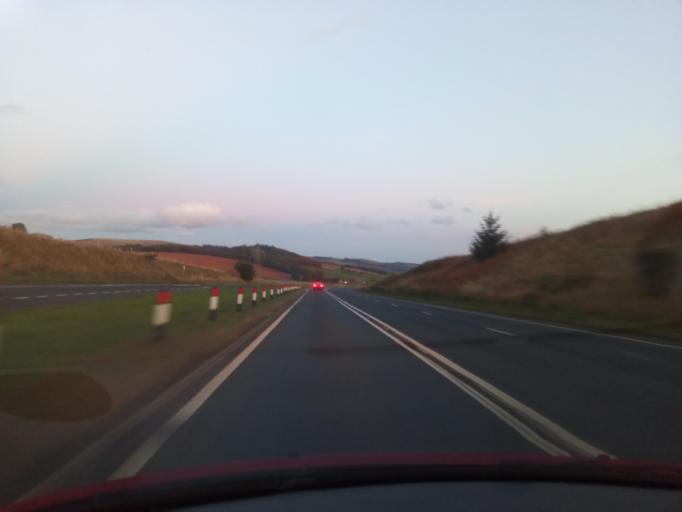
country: GB
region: Scotland
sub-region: The Scottish Borders
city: Lauder
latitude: 55.7874
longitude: -2.8262
